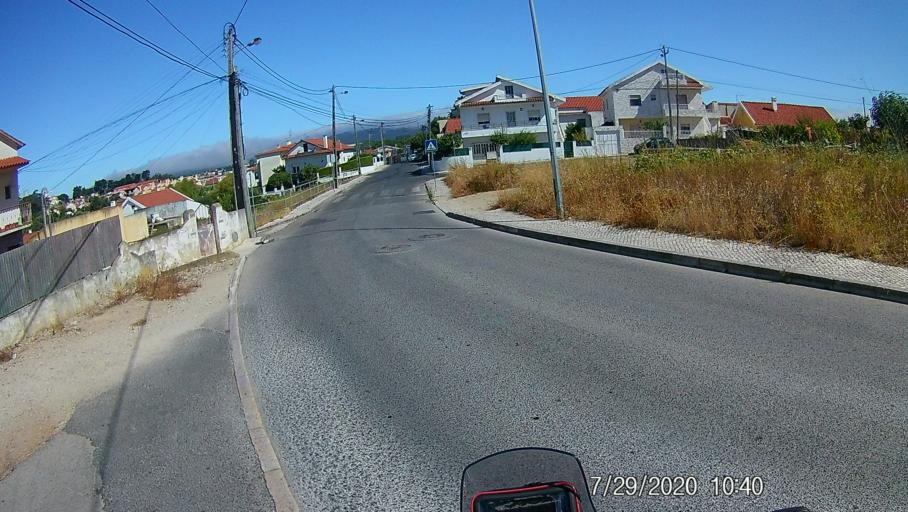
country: PT
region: Lisbon
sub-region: Cascais
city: Estoril
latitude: 38.7296
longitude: -9.3776
